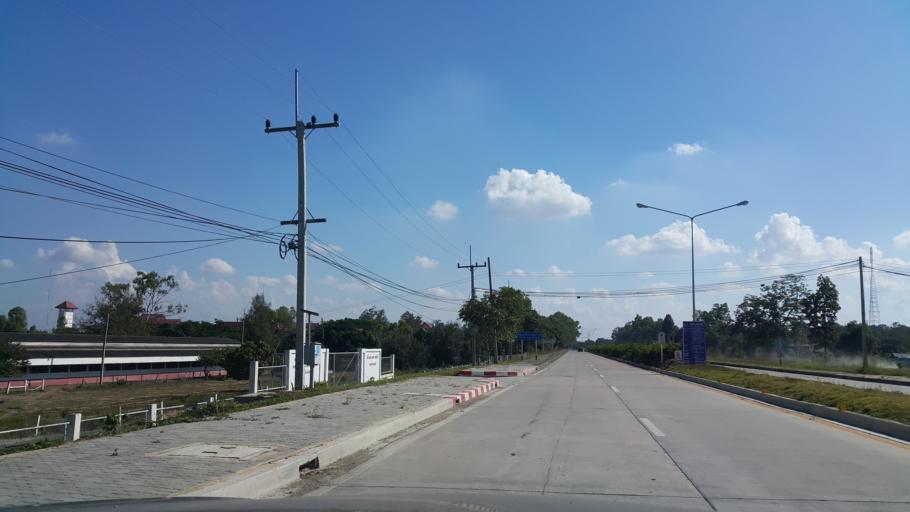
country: TH
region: Chiang Mai
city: Chiang Mai
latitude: 18.8645
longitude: 98.9594
